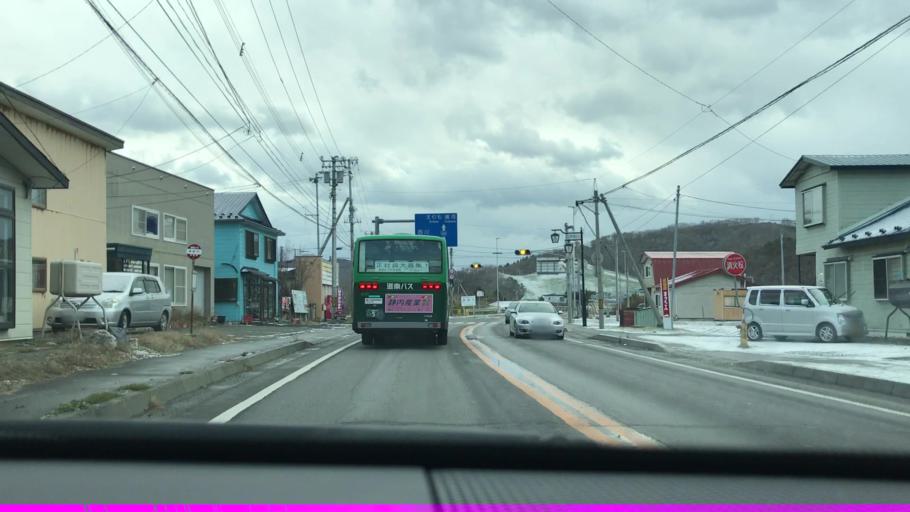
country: JP
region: Hokkaido
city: Shizunai-furukawacho
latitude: 42.3032
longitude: 142.4517
